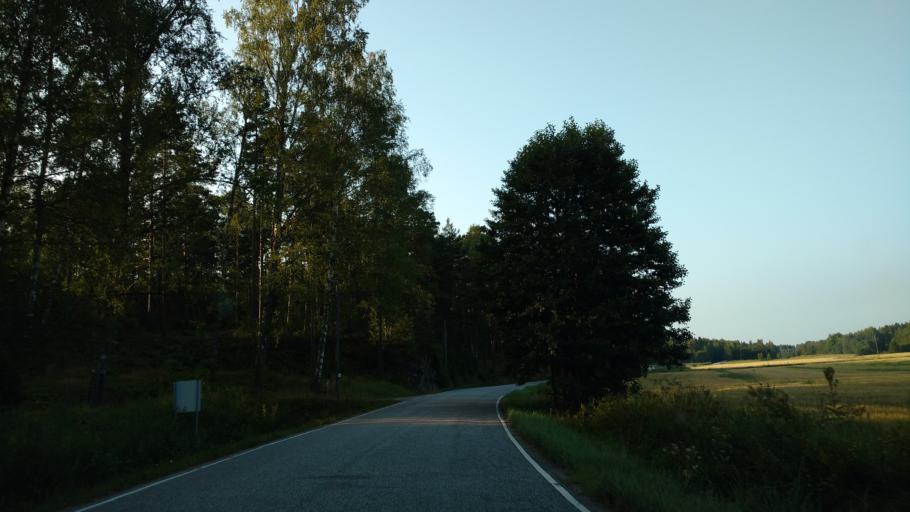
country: FI
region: Varsinais-Suomi
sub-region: Aboland-Turunmaa
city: Dragsfjaerd
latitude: 60.0370
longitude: 22.4421
